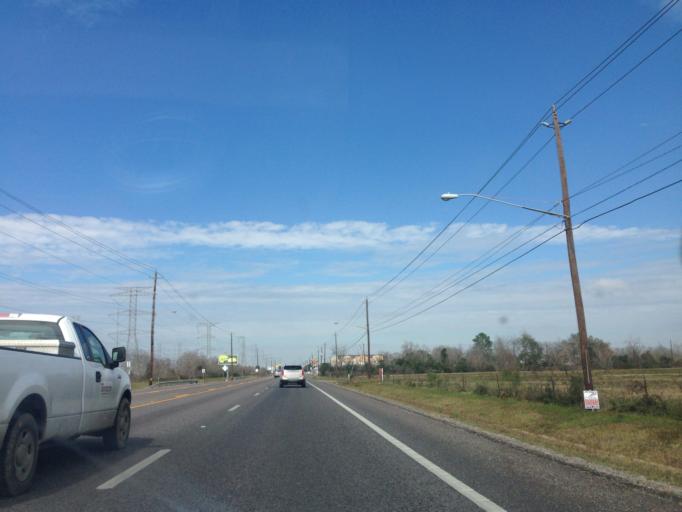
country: US
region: Texas
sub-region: Galveston County
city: Kemah
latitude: 29.5288
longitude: -95.0127
